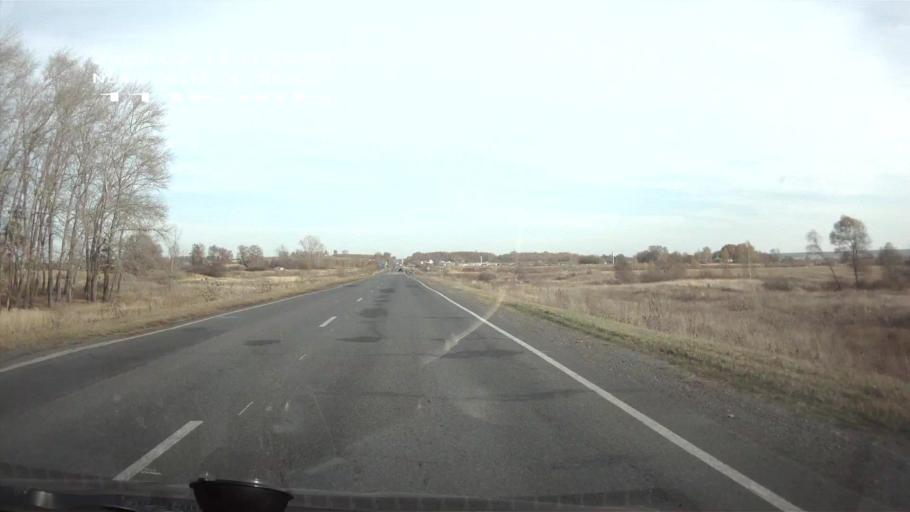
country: RU
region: Mordoviya
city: Atyashevo
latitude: 54.5541
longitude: 45.9631
